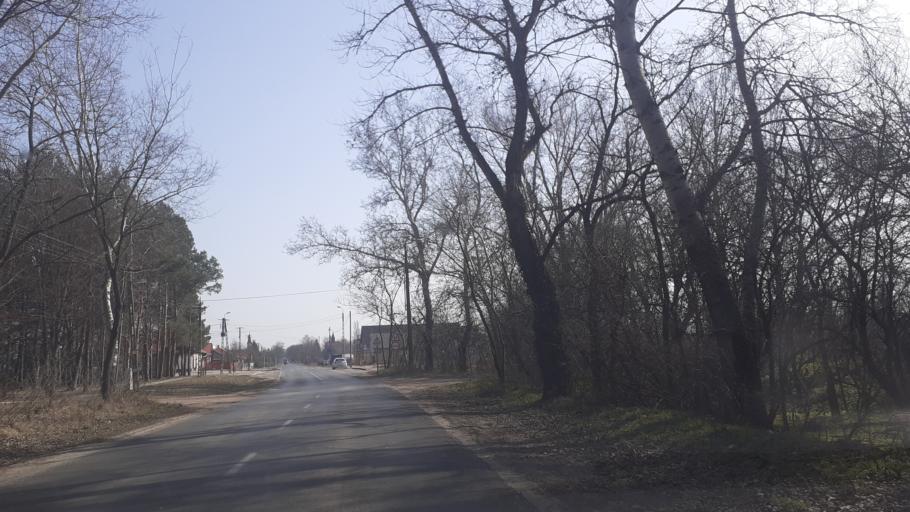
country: HU
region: Bacs-Kiskun
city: Lajosmizse
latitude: 46.9788
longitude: 19.5715
